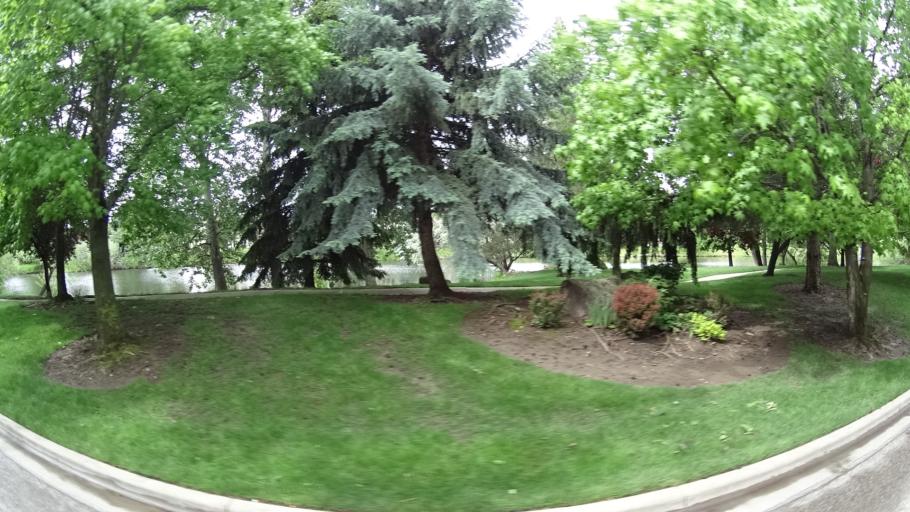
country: US
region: Idaho
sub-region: Ada County
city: Eagle
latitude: 43.6805
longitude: -116.3481
